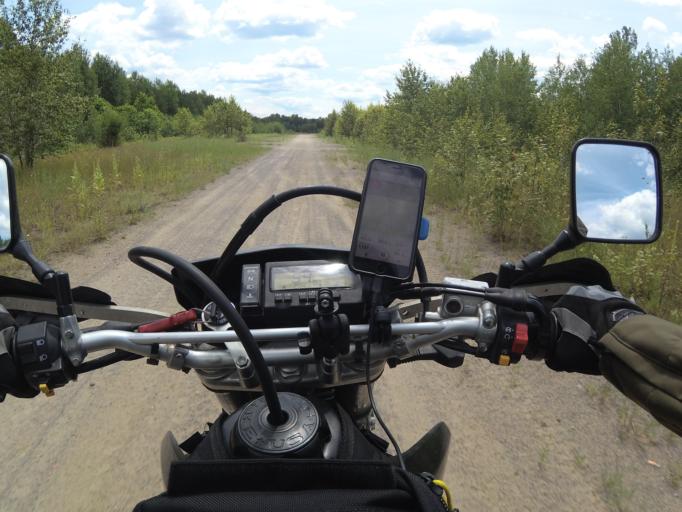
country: CA
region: Ontario
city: Bancroft
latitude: 45.0305
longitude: -77.2648
